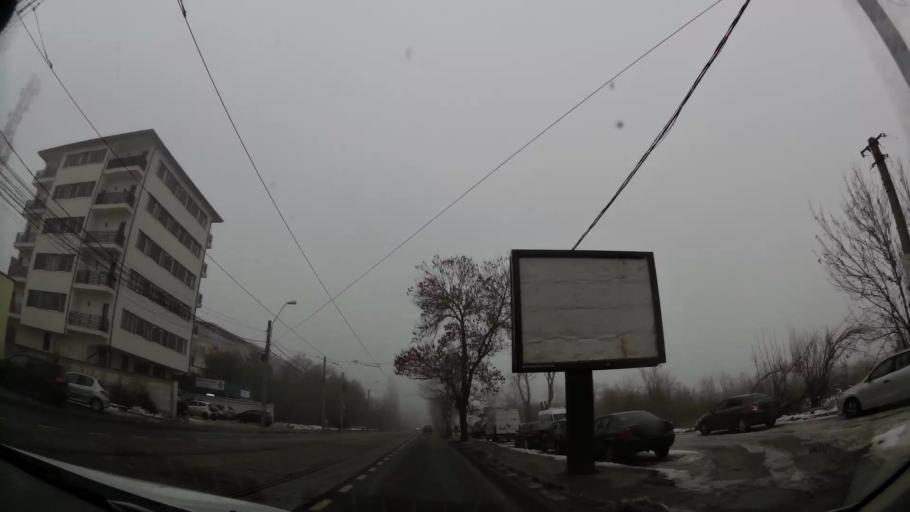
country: RO
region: Ilfov
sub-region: Comuna Chiajna
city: Rosu
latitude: 44.4686
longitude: 26.0283
